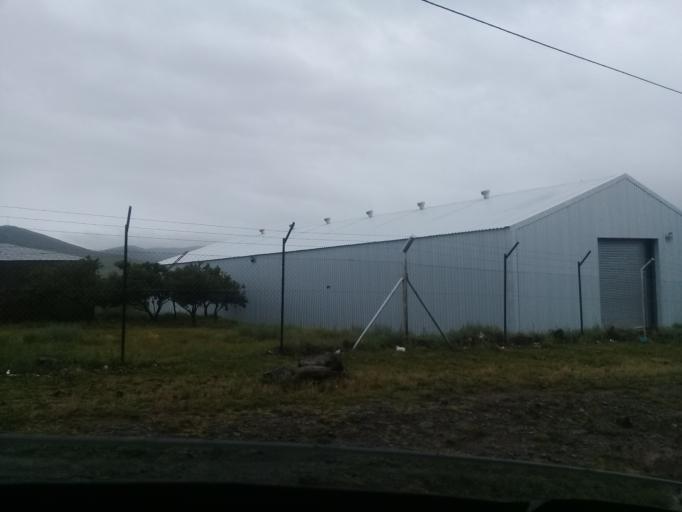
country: LS
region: Mokhotlong
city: Mokhotlong
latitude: -29.3358
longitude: 29.0325
